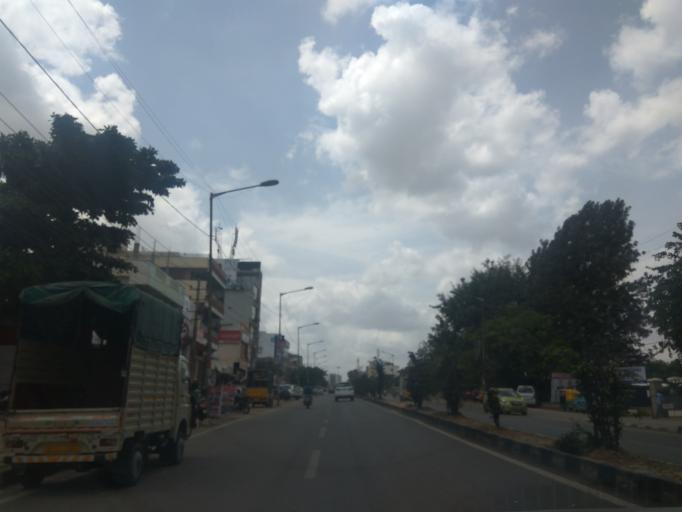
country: IN
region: Karnataka
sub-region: Bangalore Urban
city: Yelahanka
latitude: 13.0681
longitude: 77.6336
